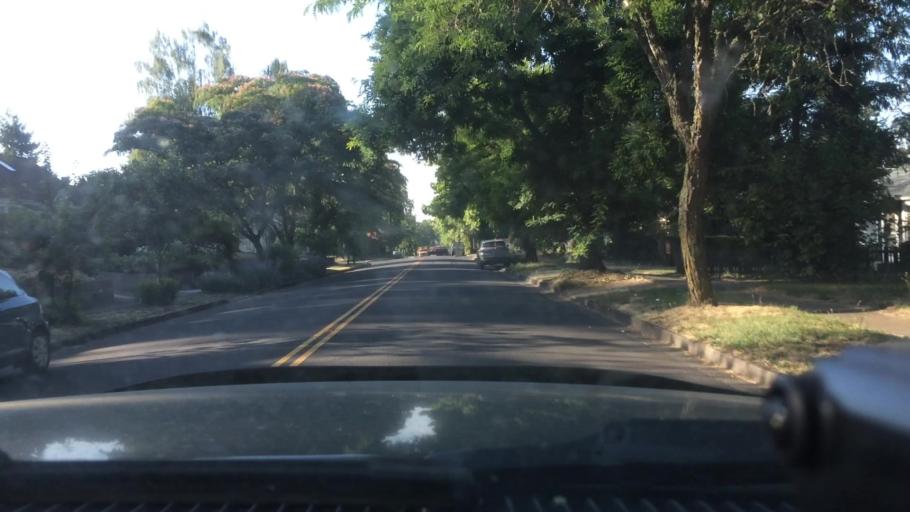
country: US
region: Oregon
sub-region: Lane County
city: Eugene
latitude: 44.0369
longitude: -123.1012
